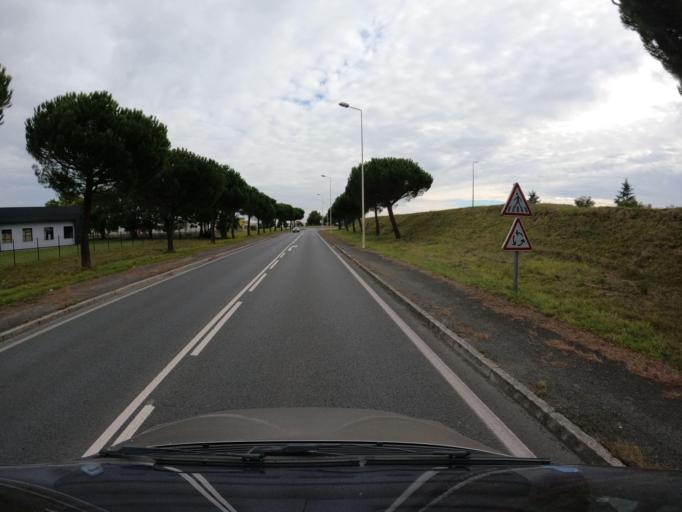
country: FR
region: Pays de la Loire
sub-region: Departement de la Loire-Atlantique
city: Getigne
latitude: 47.0849
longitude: -1.2593
